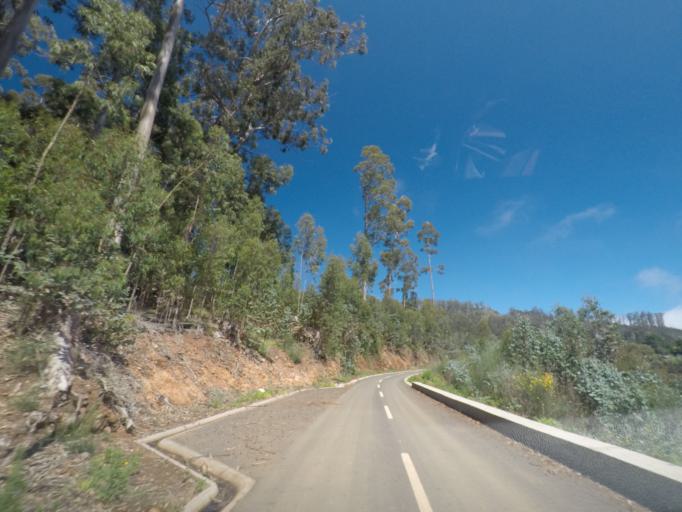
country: PT
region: Madeira
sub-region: Calheta
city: Arco da Calheta
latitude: 32.7245
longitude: -17.1224
